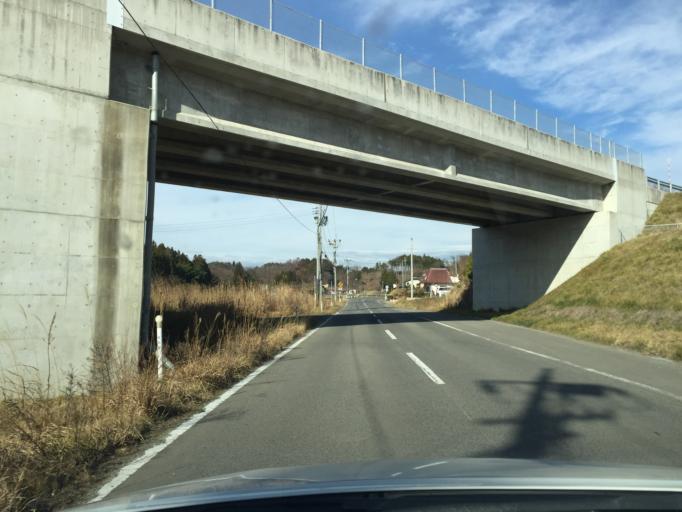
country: JP
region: Fukushima
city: Ishikawa
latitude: 37.2547
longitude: 140.5637
